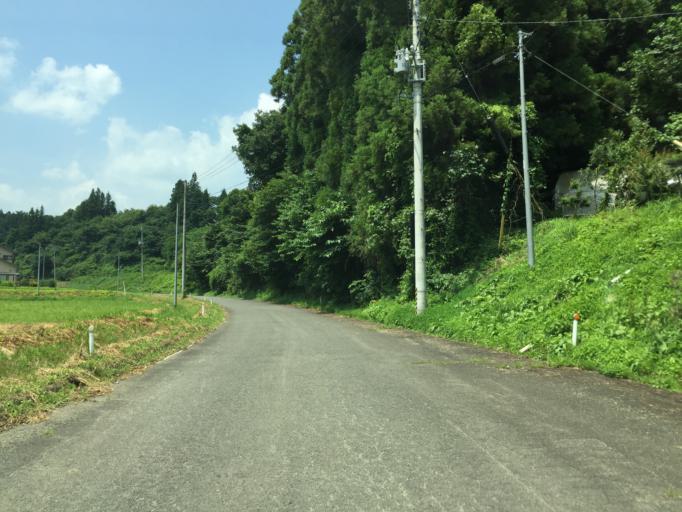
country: JP
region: Fukushima
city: Ishikawa
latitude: 37.2240
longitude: 140.5502
